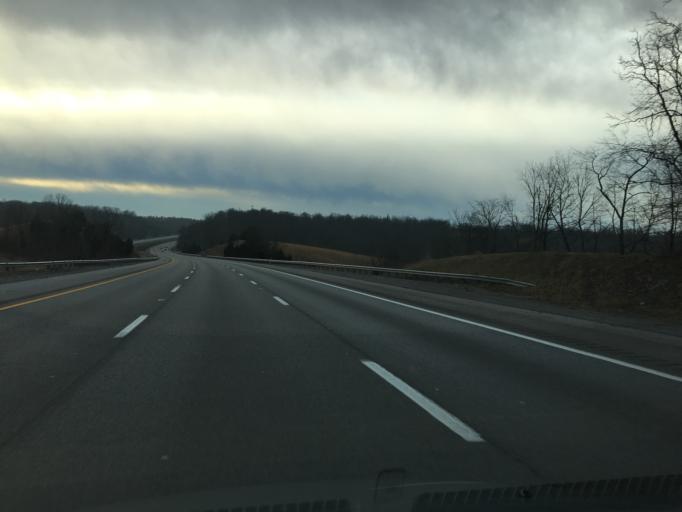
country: US
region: Kentucky
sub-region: Grant County
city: Williamstown
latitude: 38.4545
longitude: -84.5752
